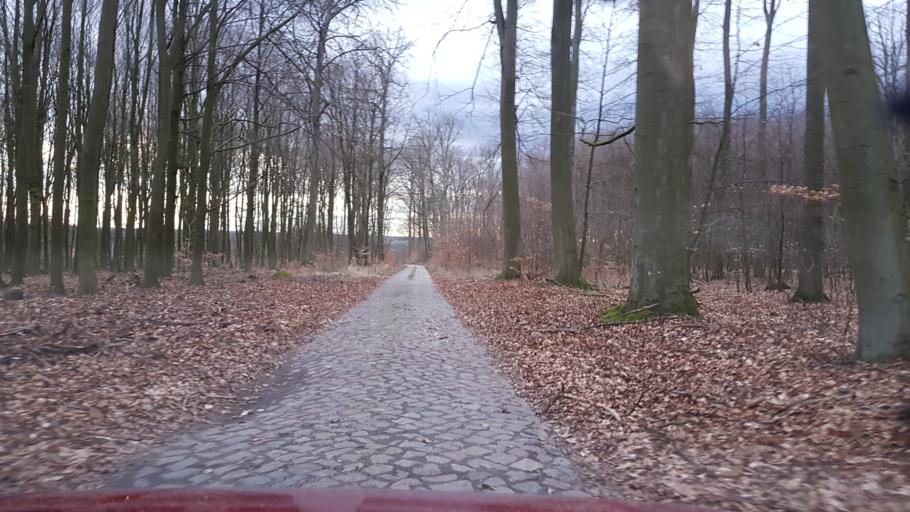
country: PL
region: West Pomeranian Voivodeship
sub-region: Powiat gryfinski
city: Stare Czarnowo
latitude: 53.2987
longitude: 14.7268
